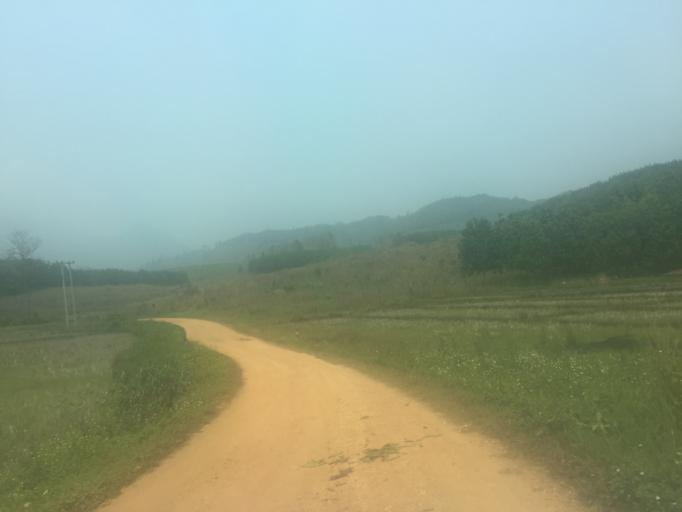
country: TH
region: Phayao
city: Phu Sang
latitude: 19.7720
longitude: 100.5378
